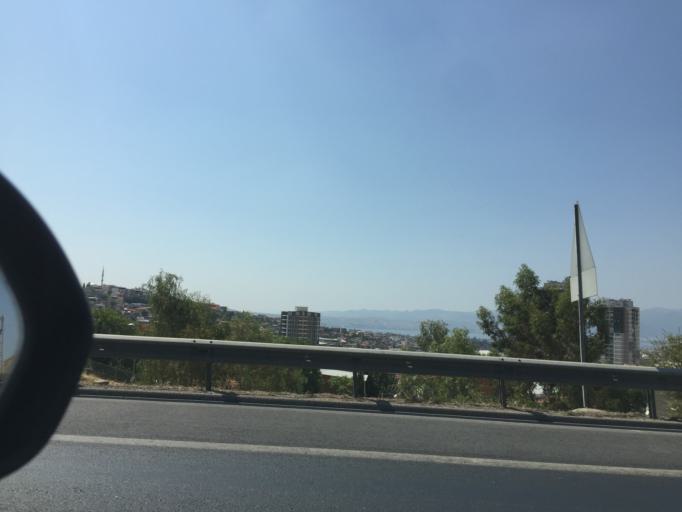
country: TR
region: Izmir
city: Karsiyaka
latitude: 38.4861
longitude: 27.1324
